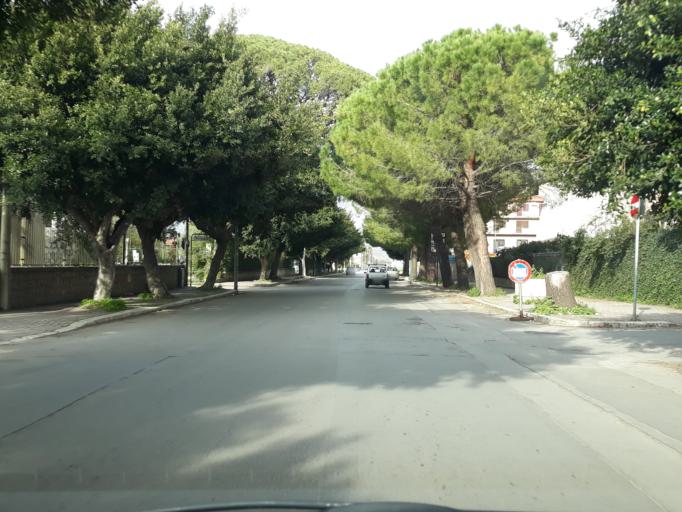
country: IT
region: Sicily
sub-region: Palermo
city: Partinico
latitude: 38.0513
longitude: 13.1249
